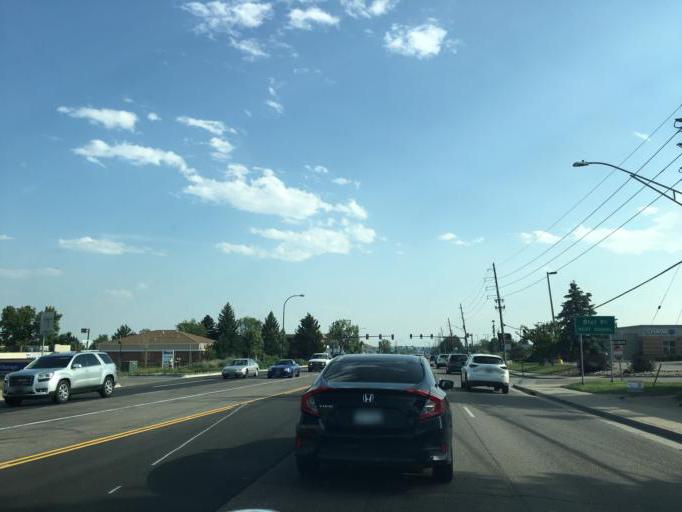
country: US
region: Colorado
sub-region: Adams County
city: Westminster
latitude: 39.8455
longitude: -105.0533
